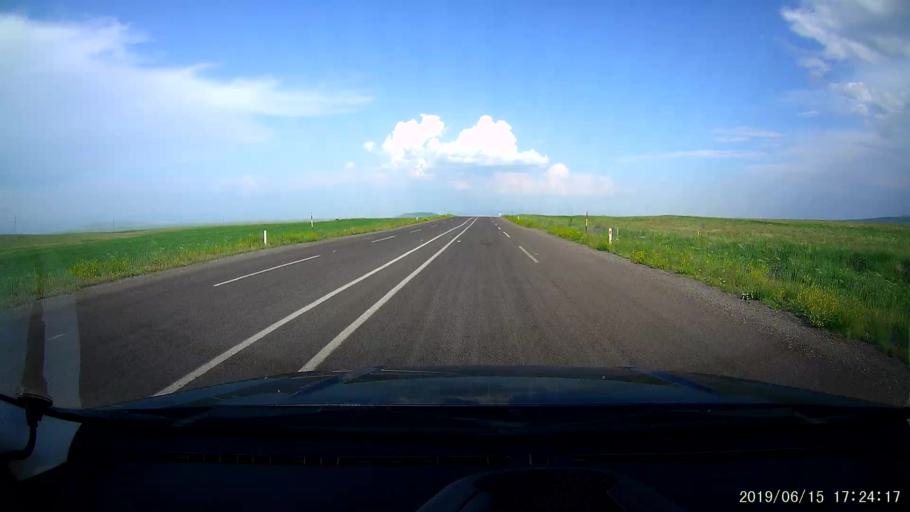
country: TR
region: Kars
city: Basgedikler
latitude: 40.6148
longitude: 43.3799
